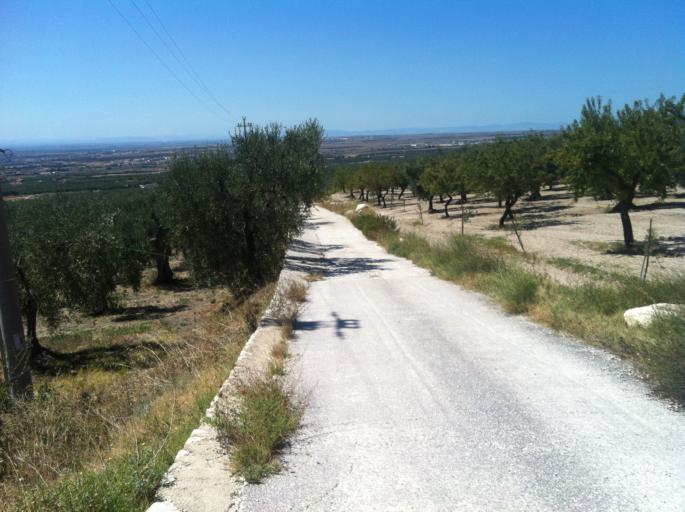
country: IT
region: Apulia
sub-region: Provincia di Foggia
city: Manfredonia
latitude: 41.6622
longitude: 15.9170
